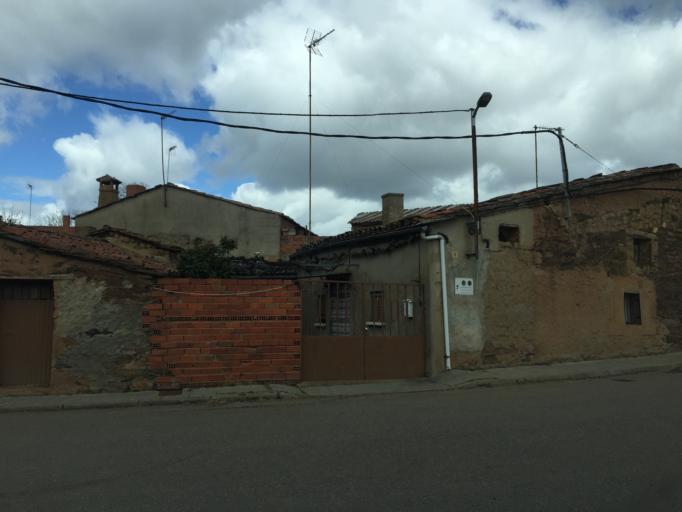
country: ES
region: Castille and Leon
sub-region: Provincia de Zamora
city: Manzanal del Barco
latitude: 41.5836
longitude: -5.9619
